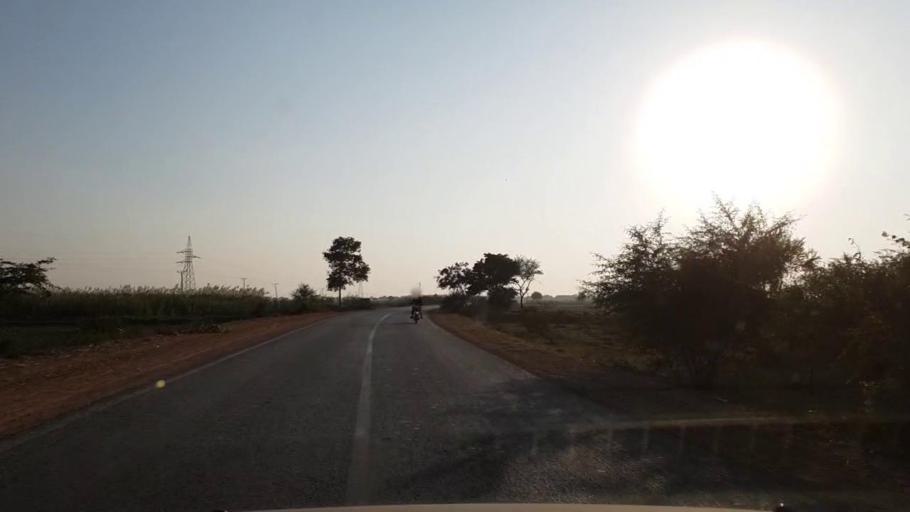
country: PK
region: Sindh
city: Daro Mehar
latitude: 24.6538
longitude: 68.1286
